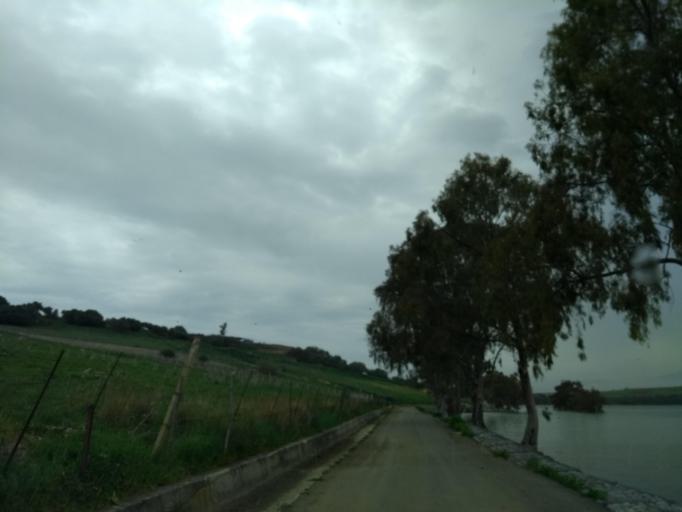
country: IT
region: Sicily
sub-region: Palermo
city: Partinico
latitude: 37.9931
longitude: 13.0823
